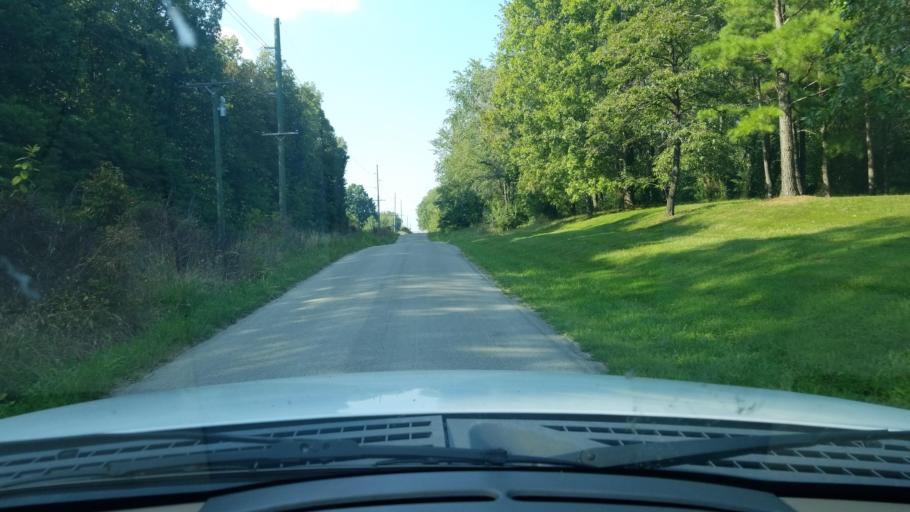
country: US
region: Illinois
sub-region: Saline County
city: Harrisburg
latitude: 37.8431
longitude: -88.5964
